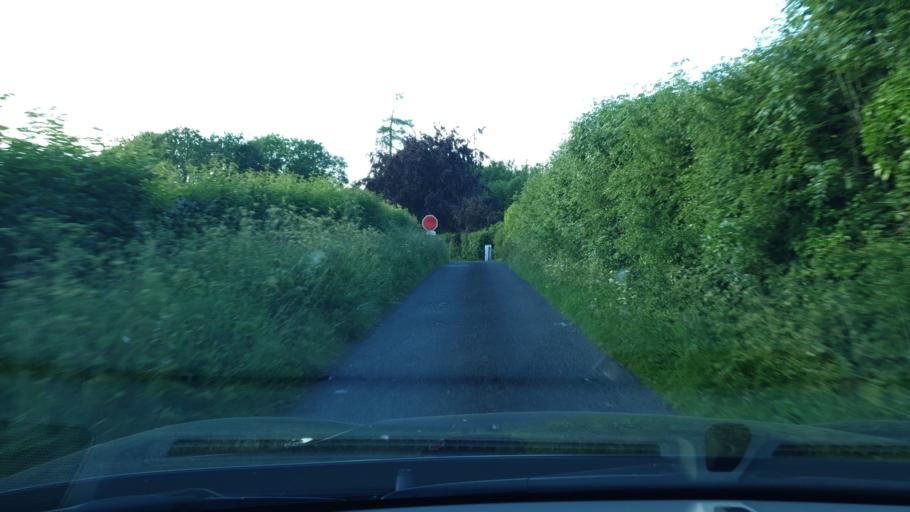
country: IE
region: Leinster
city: Hartstown
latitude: 53.4477
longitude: -6.4104
